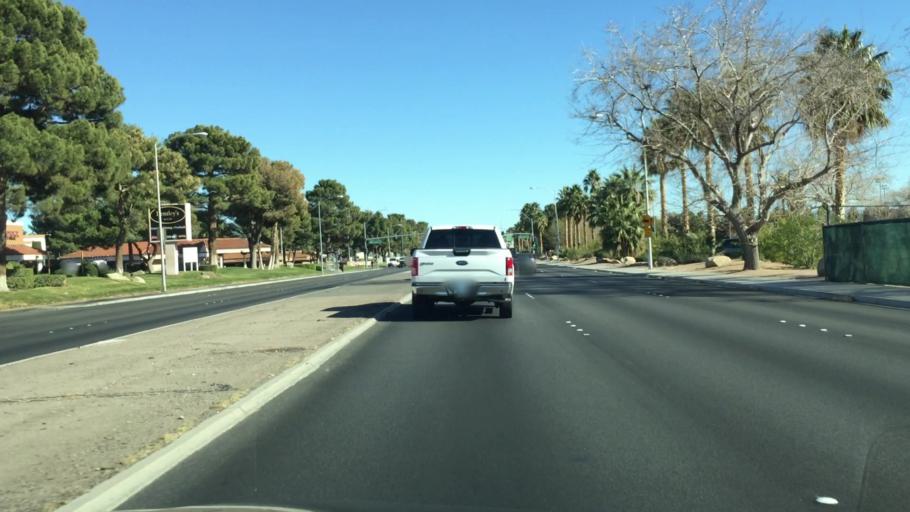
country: US
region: Nevada
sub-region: Clark County
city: Whitney
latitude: 36.0715
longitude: -115.1149
